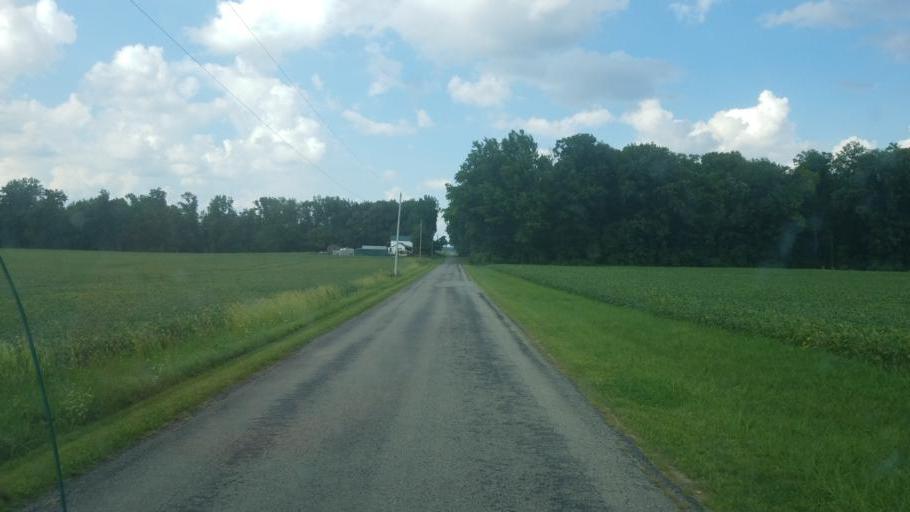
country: US
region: Ohio
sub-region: Huron County
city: Plymouth
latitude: 40.9994
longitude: -82.7085
